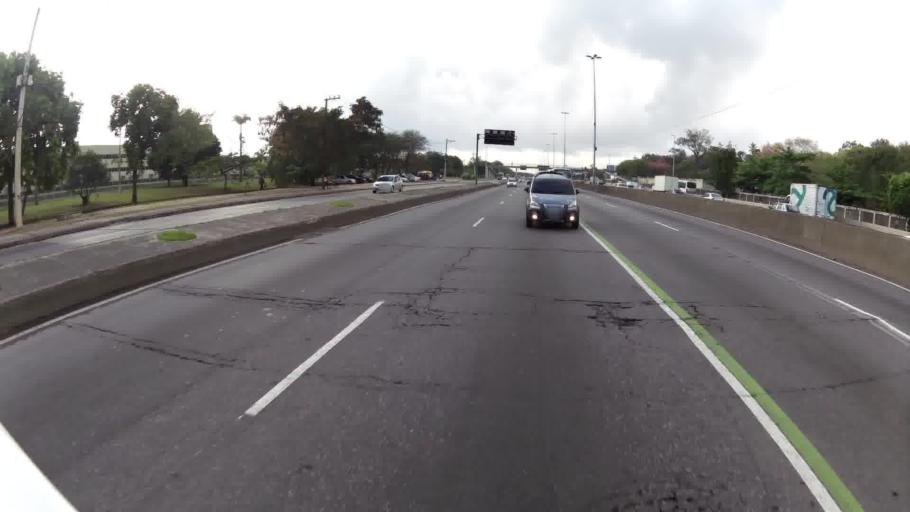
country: BR
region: Rio de Janeiro
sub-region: Duque De Caxias
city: Duque de Caxias
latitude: -22.8324
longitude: -43.2664
